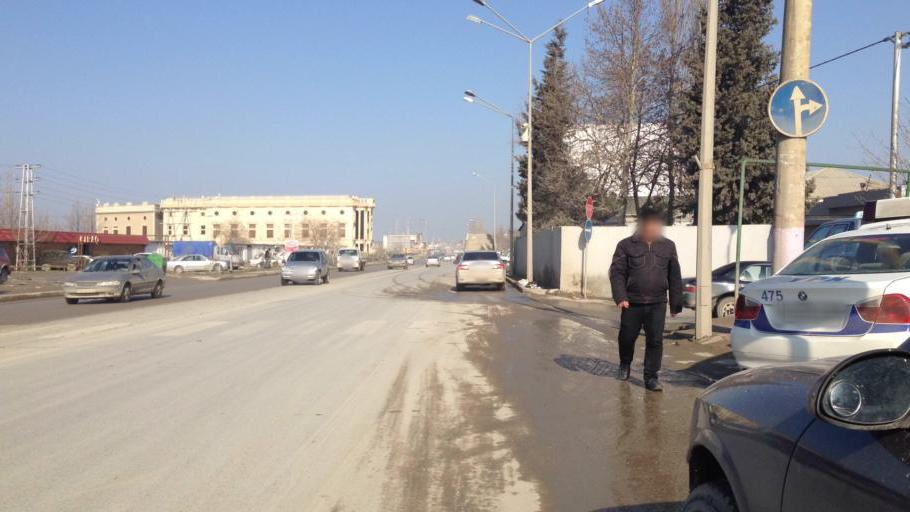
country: AZ
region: Baki
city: Binagadi
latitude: 40.4433
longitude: 49.8446
